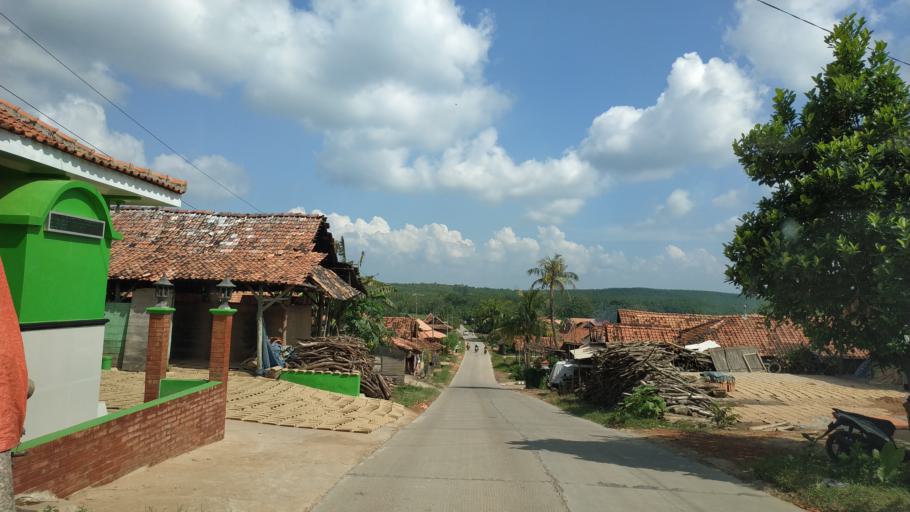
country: ID
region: Central Java
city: Jepang
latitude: -7.0123
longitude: 111.1173
